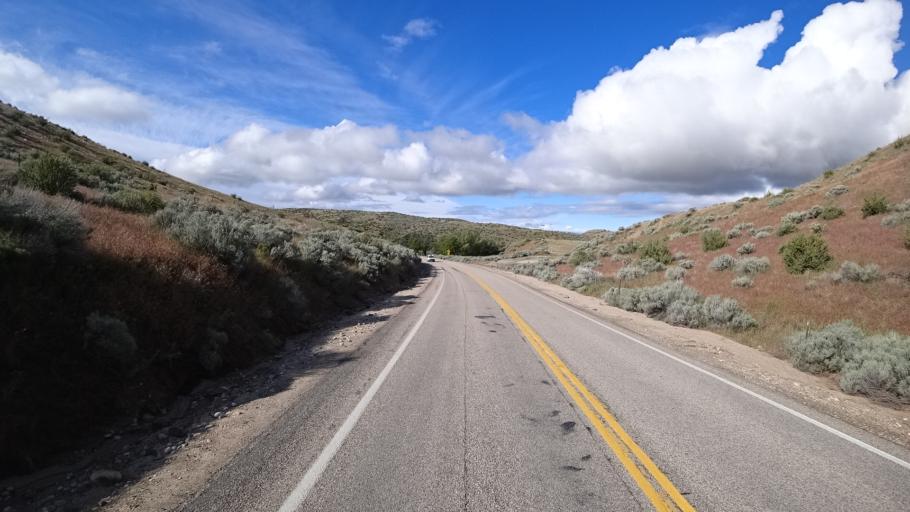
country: US
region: Idaho
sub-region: Ada County
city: Garden City
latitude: 43.7006
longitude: -116.2608
